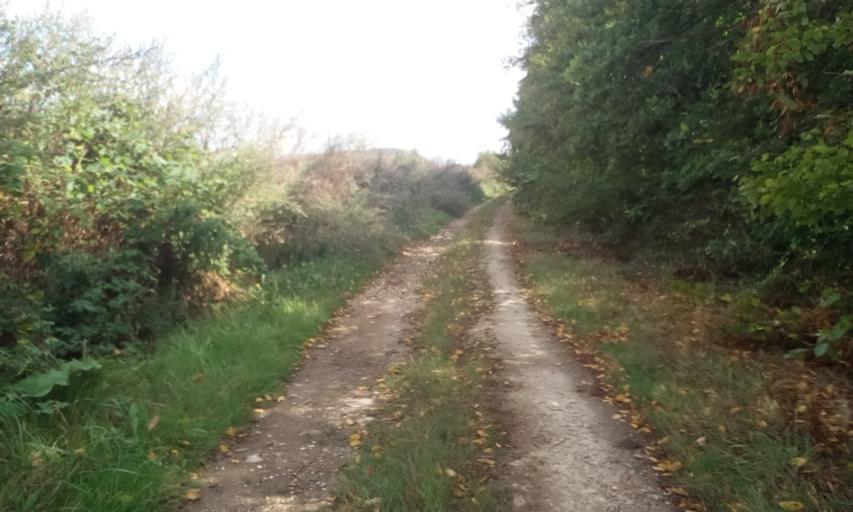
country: FR
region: Lower Normandy
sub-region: Departement du Calvados
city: Cagny
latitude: 49.1157
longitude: -0.2572
